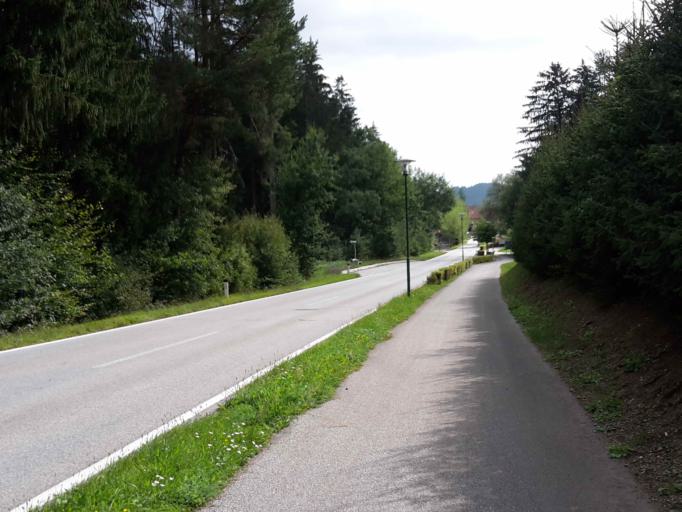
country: AT
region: Carinthia
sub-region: Politischer Bezirk Volkermarkt
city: Eberndorf
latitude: 46.6111
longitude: 14.5944
